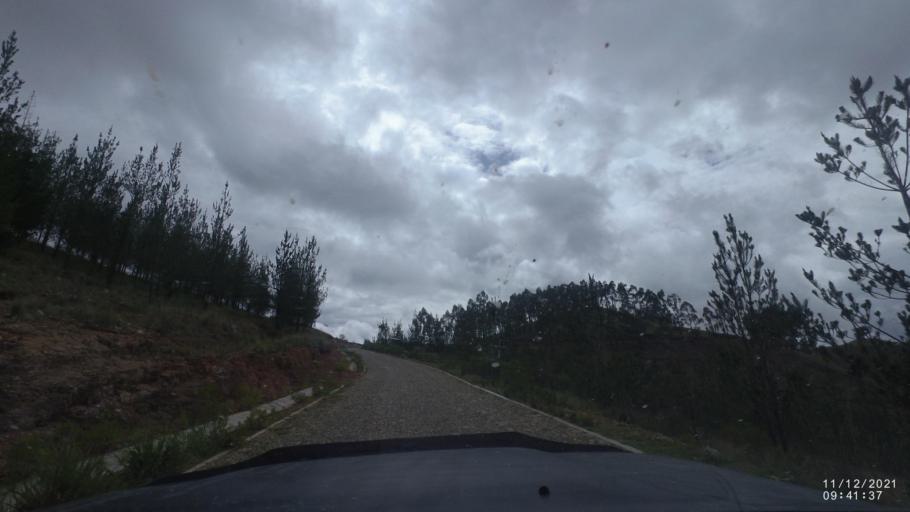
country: BO
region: Cochabamba
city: Tarata
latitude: -17.8122
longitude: -65.9780
